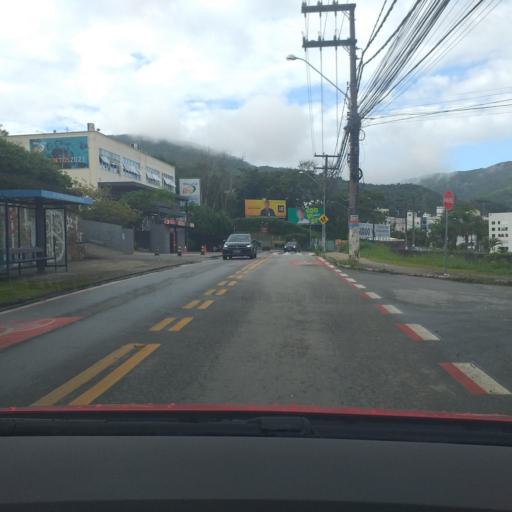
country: BR
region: Santa Catarina
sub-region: Florianopolis
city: Corrego Grande
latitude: -27.5994
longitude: -48.4989
